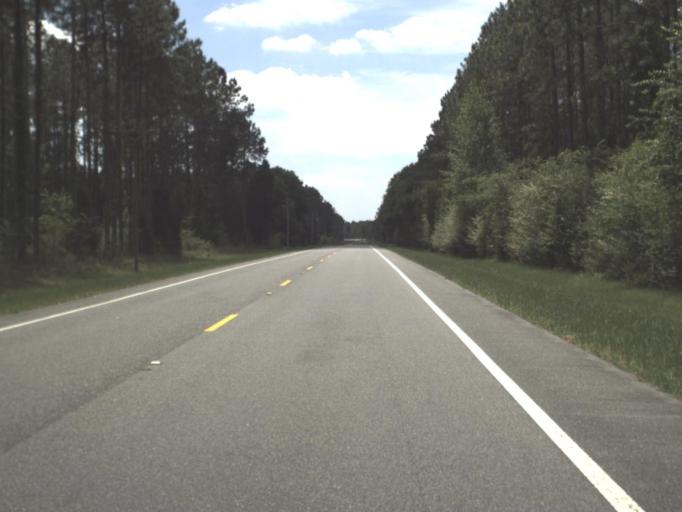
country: US
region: Florida
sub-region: Calhoun County
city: Blountstown
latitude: 30.3393
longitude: -85.1196
